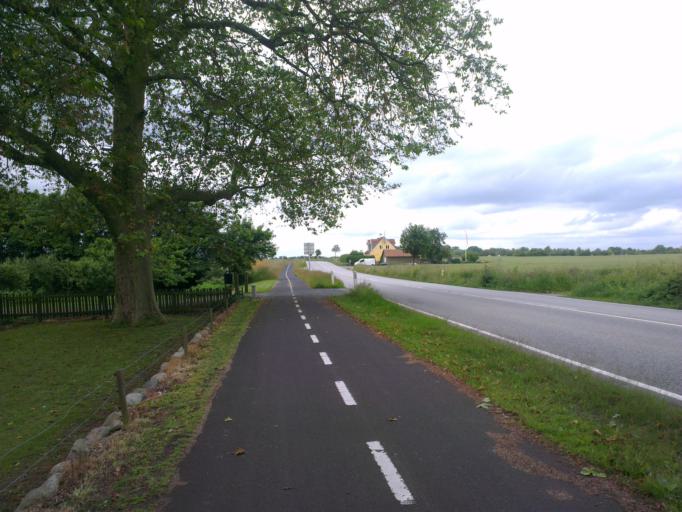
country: DK
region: Capital Region
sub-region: Frederikssund Kommune
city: Skibby
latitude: 55.6902
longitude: 11.9497
